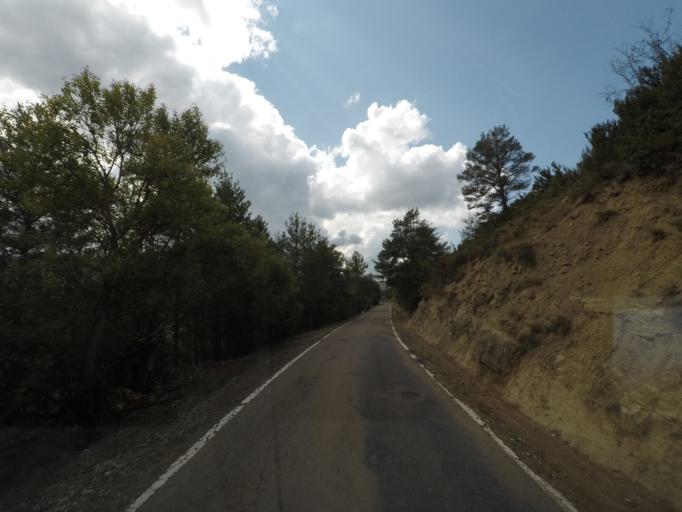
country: ES
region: Aragon
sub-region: Provincia de Huesca
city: Yebra de Basa
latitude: 42.3933
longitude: -0.2957
